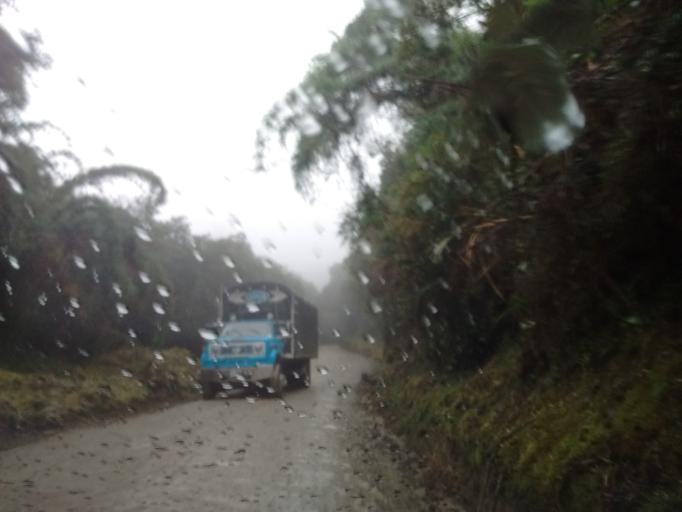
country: CO
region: Cauca
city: Paispamba
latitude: 2.1661
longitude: -76.4177
